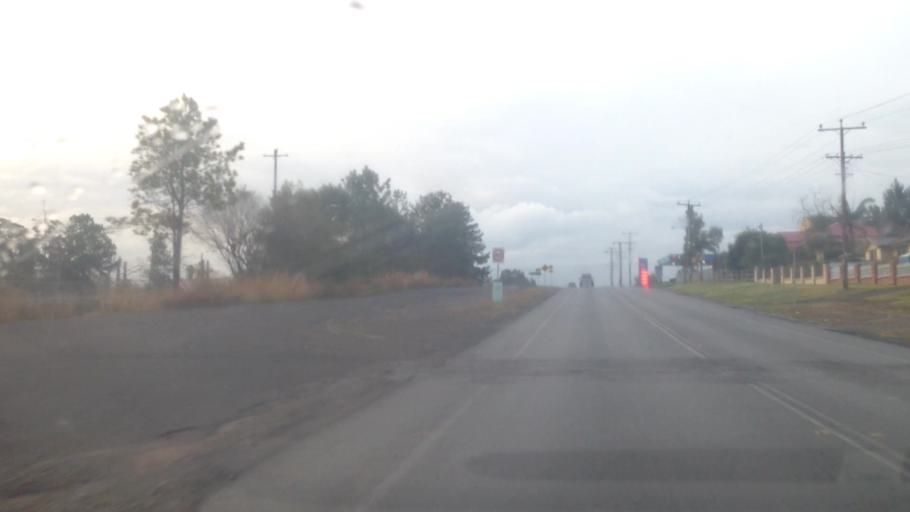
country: AU
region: New South Wales
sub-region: Wyong Shire
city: Charmhaven
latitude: -33.1775
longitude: 151.4873
